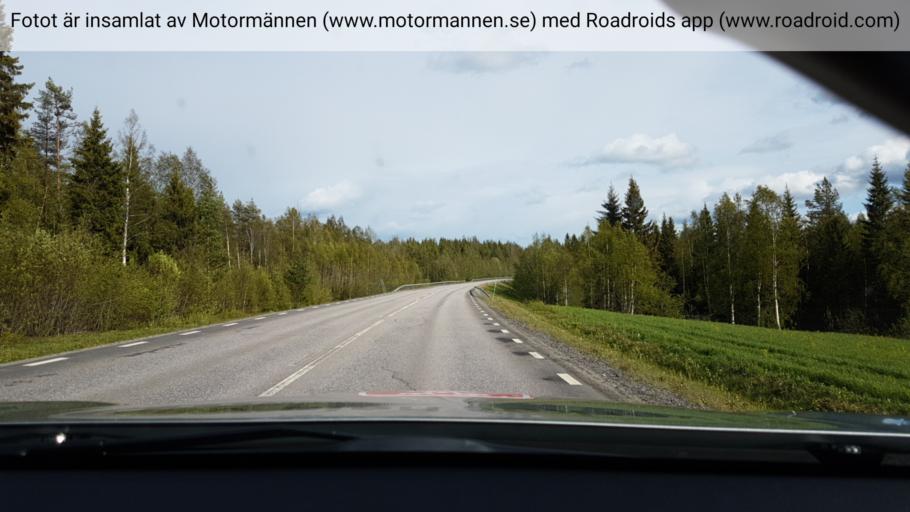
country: SE
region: Vaesterbotten
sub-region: Vannas Kommun
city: Vaennaes
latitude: 63.9193
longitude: 19.6390
